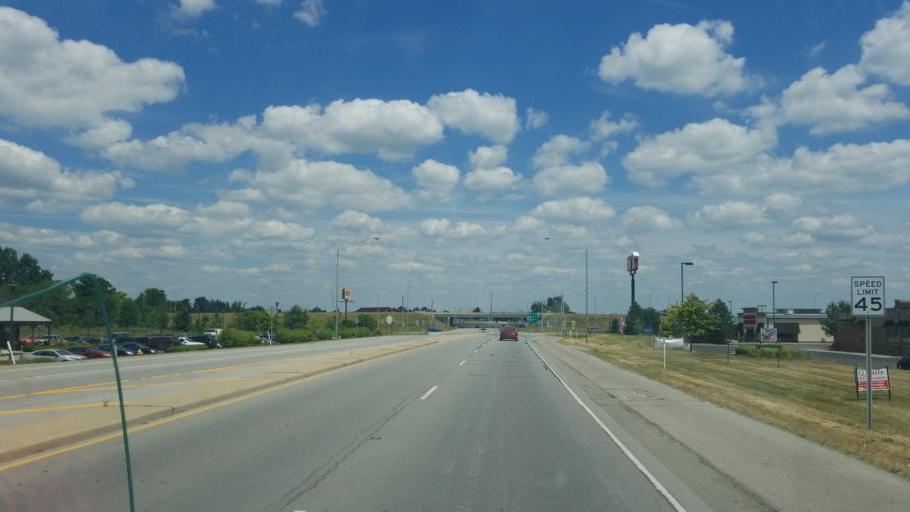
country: US
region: Indiana
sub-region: Allen County
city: New Haven
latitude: 41.1310
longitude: -85.0099
